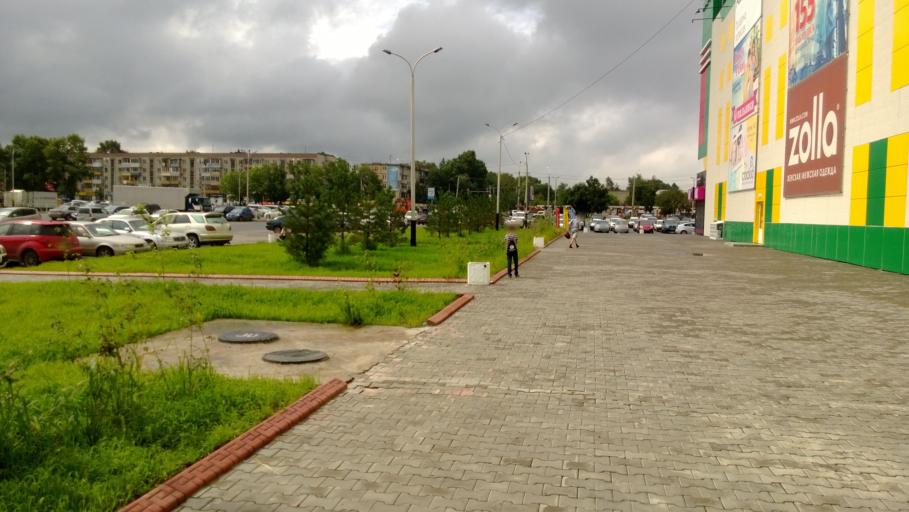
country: RU
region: Khabarovsk Krai
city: Khabarovsk Vtoroy
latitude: 48.3958
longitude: 135.1074
